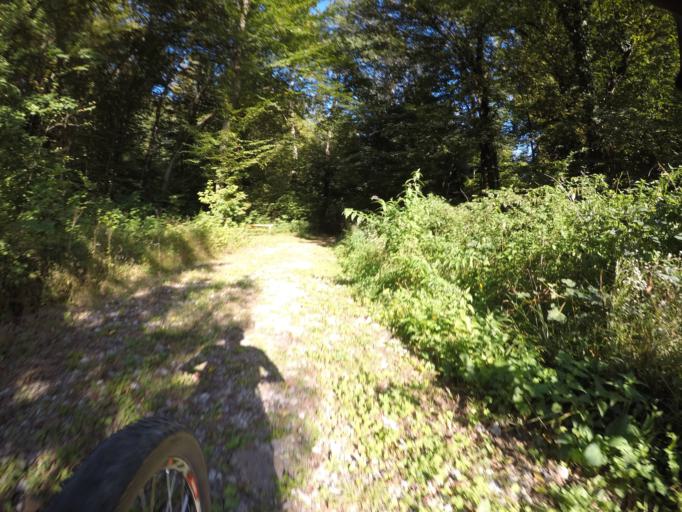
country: AT
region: Lower Austria
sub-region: Politischer Bezirk Bruck an der Leitha
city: Mannersdorf am Leithagebirge
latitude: 47.9584
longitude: 16.6092
